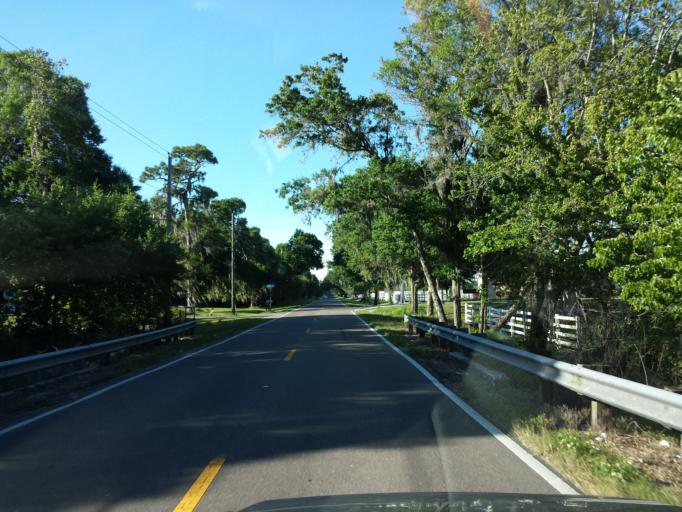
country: US
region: Florida
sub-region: Hillsborough County
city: Dover
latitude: 28.0330
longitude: -82.2365
